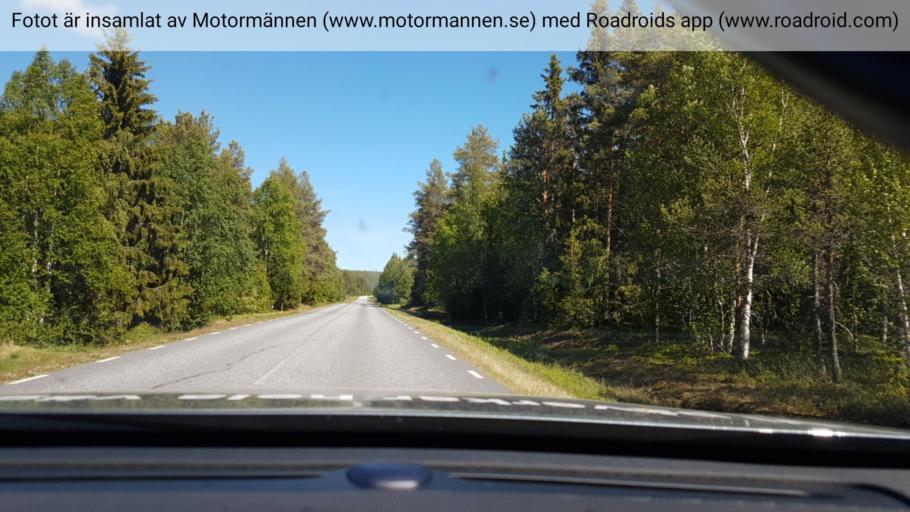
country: SE
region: Vaesterbotten
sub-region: Vilhelmina Kommun
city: Vilhelmina
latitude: 64.6300
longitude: 16.8933
